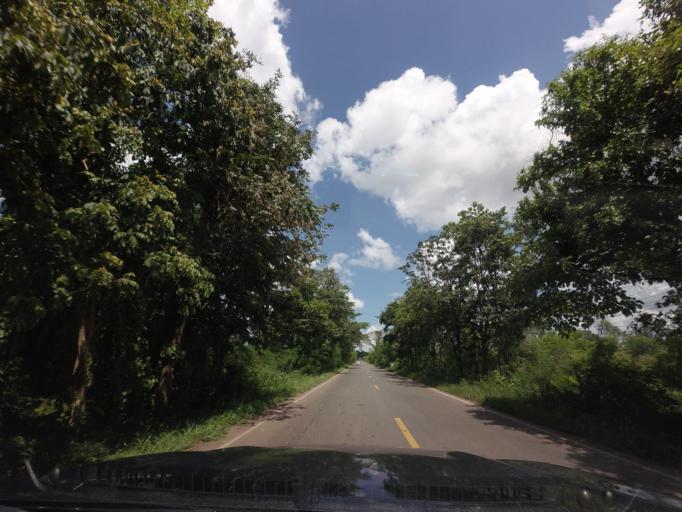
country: TH
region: Changwat Udon Thani
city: Ban Dung
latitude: 17.6732
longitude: 103.1745
